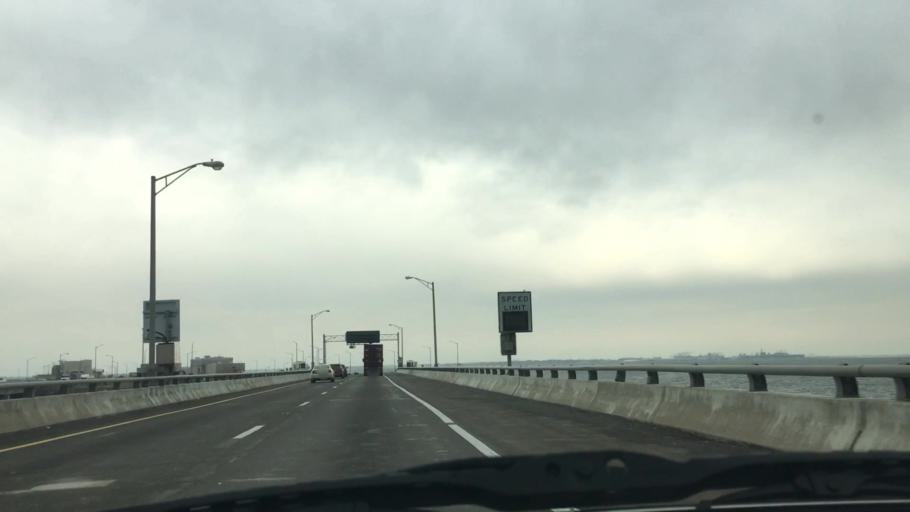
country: US
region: Virginia
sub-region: City of Hampton
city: East Hampton
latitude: 37.0044
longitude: -76.3206
